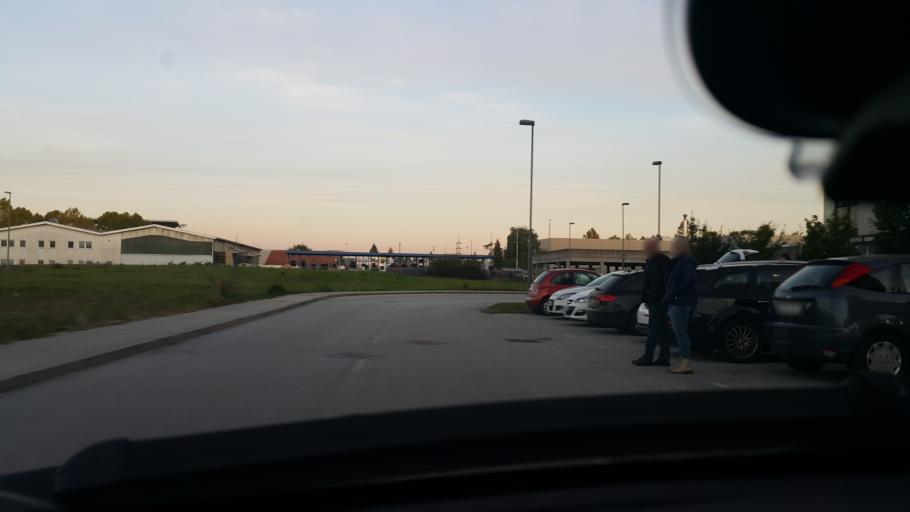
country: SI
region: Maribor
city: Maribor
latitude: 46.5385
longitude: 15.6405
